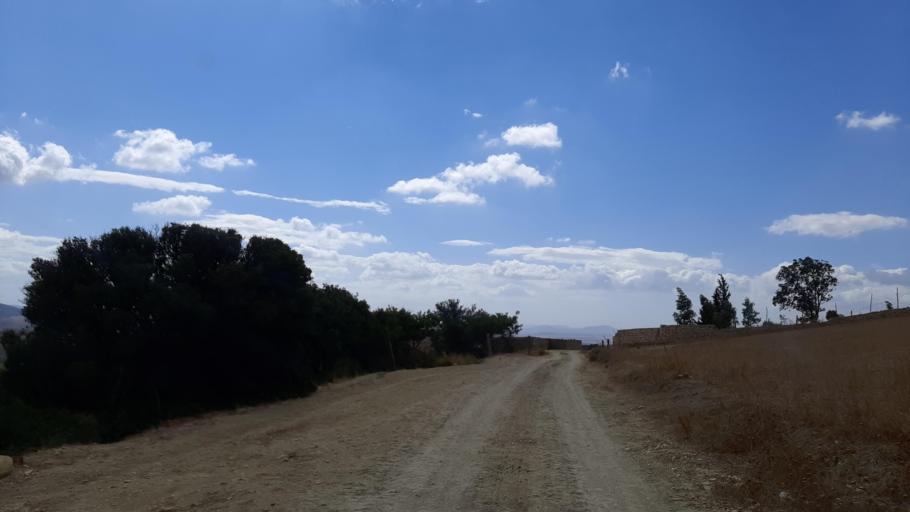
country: TN
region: Zaghwan
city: Zaghouan
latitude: 36.4913
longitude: 10.1768
